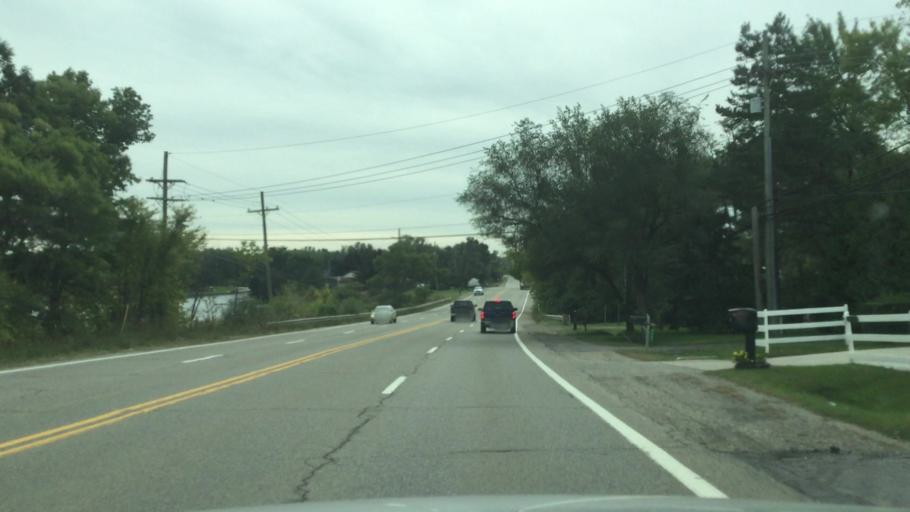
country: US
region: Michigan
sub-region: Oakland County
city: Clarkston
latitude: 42.7643
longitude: -83.4849
